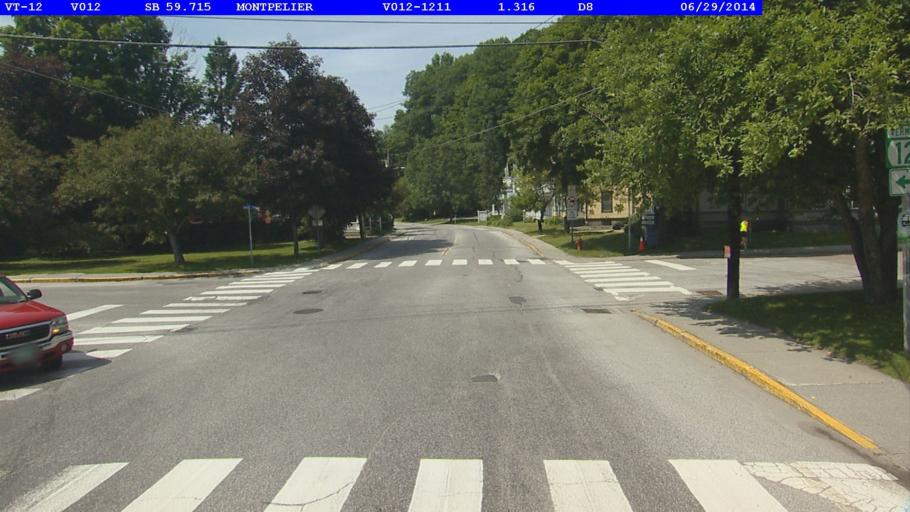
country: US
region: Vermont
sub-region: Washington County
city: Montpelier
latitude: 44.2639
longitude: -72.5724
